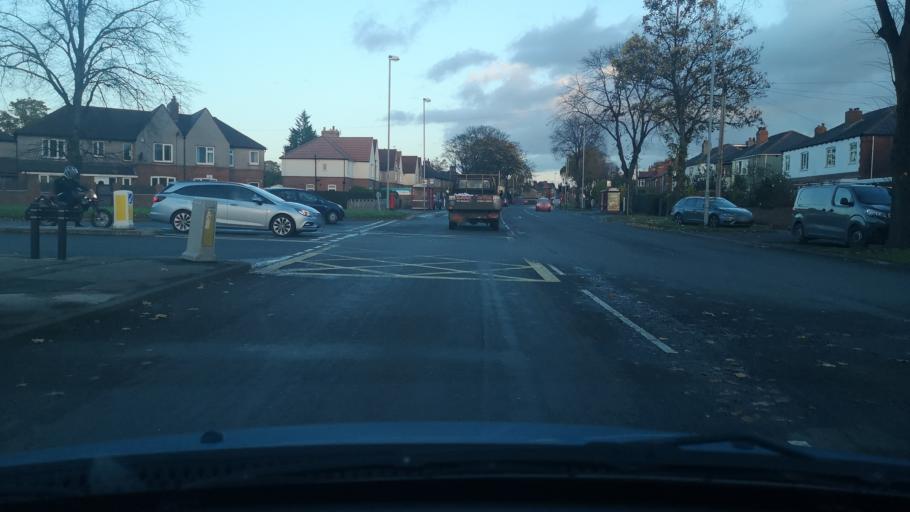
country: GB
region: England
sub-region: City and Borough of Wakefield
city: Crigglestone
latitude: 53.6690
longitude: -1.5334
